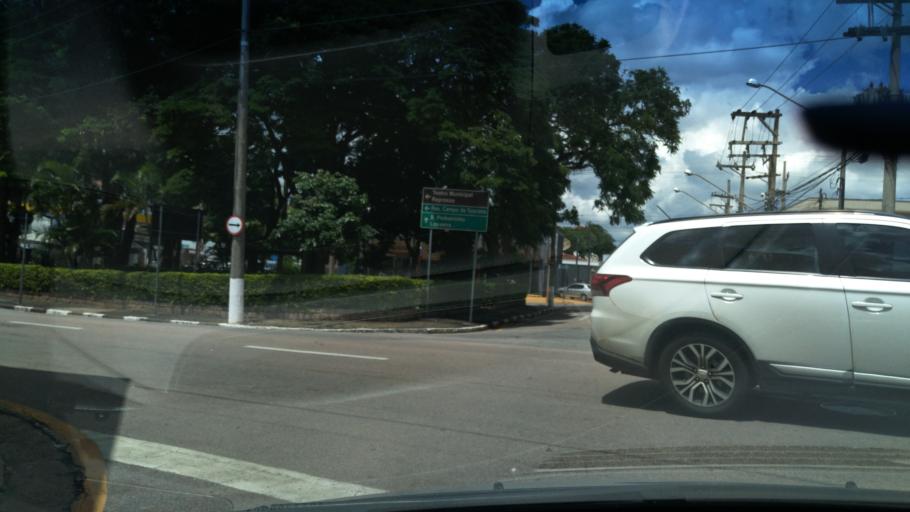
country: BR
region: Sao Paulo
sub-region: Vinhedo
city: Vinhedo
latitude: -23.0332
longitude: -46.9777
